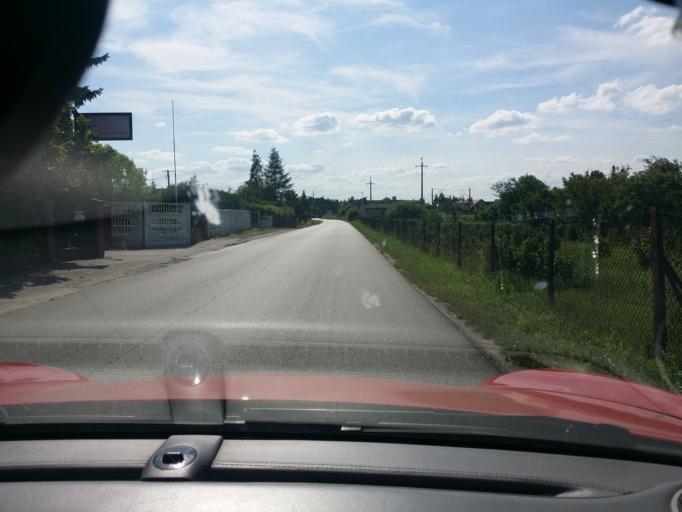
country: PL
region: Masovian Voivodeship
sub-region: Powiat radomski
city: Kowala
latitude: 51.3469
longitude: 21.0889
